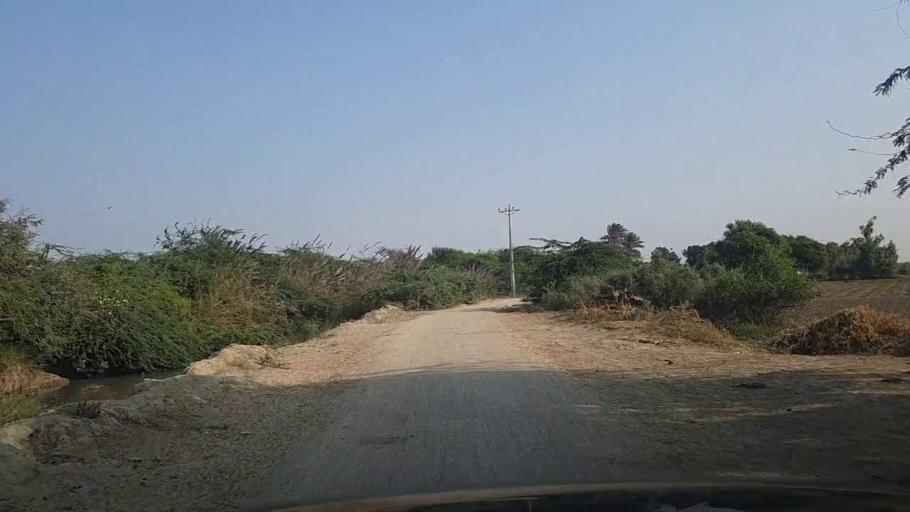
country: PK
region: Sindh
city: Mirpur Sakro
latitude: 24.6337
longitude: 67.7553
